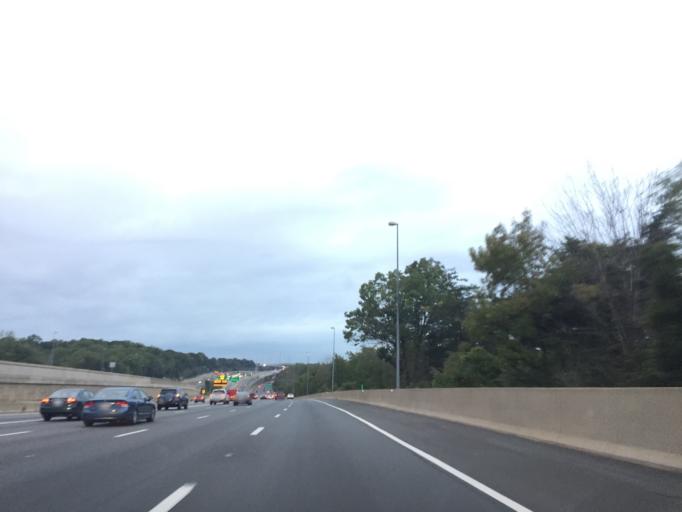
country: US
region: Virginia
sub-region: Fairfax County
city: Franconia
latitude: 38.7937
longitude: -77.1538
